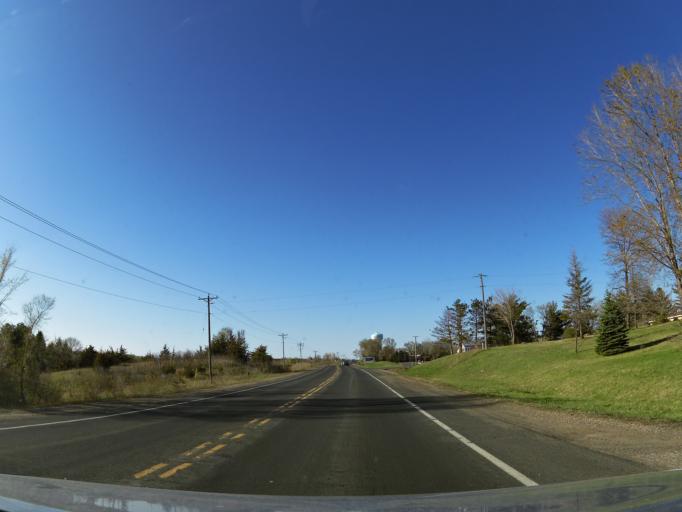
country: US
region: Wisconsin
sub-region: Saint Croix County
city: Hudson
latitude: 44.9730
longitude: -92.7213
